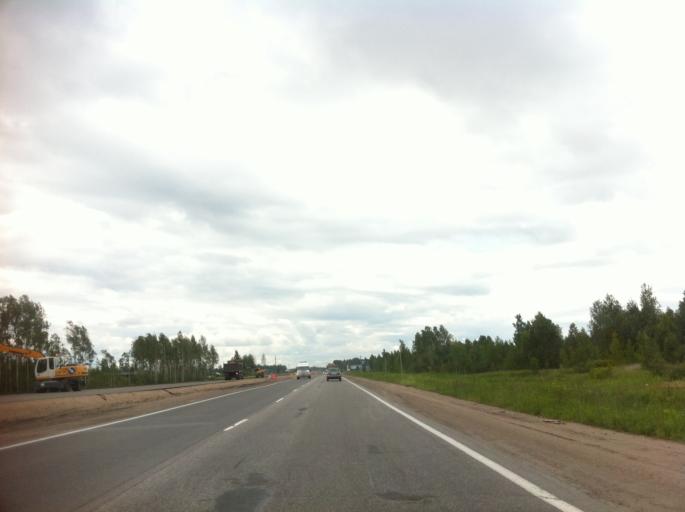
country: RU
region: Leningrad
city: Gatchina
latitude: 59.5686
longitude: 30.1683
